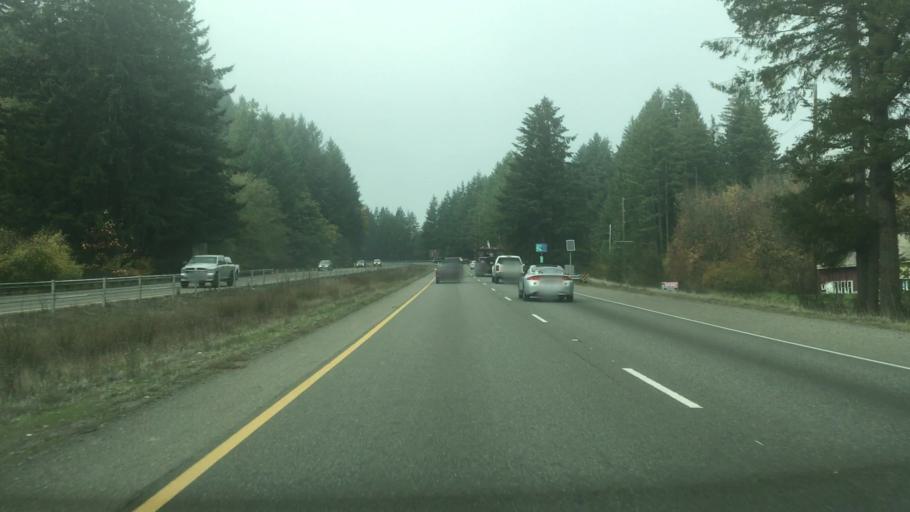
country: US
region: Washington
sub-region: Thurston County
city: Olympia
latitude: 47.0529
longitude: -123.0028
